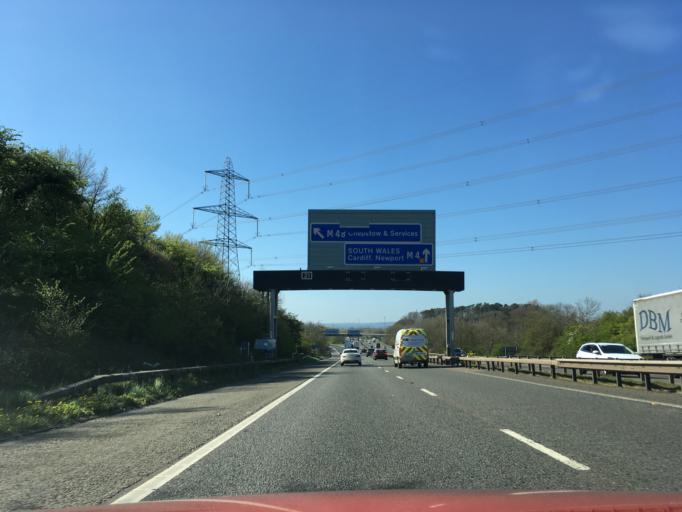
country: GB
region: England
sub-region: South Gloucestershire
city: Almondsbury
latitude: 51.5673
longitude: -2.5730
